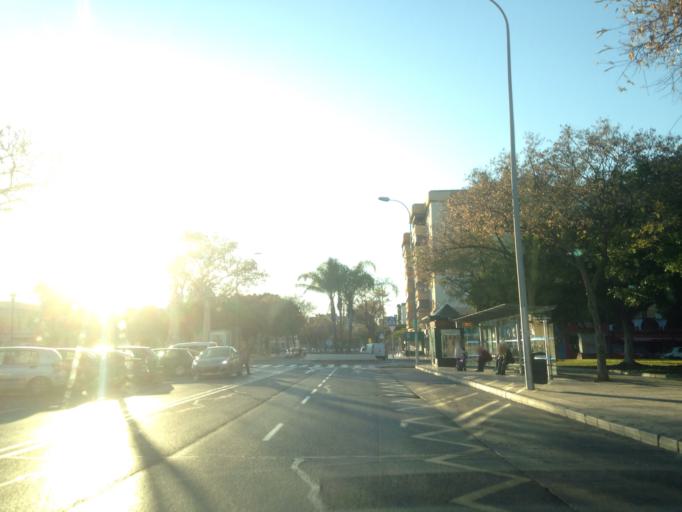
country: ES
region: Andalusia
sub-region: Provincia de Malaga
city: Malaga
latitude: 36.6882
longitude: -4.4476
